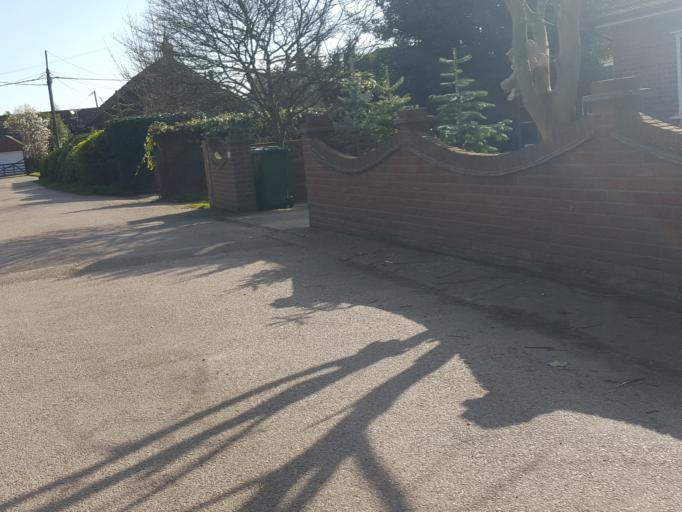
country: GB
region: England
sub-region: Essex
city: Little Clacton
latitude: 51.8596
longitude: 1.1144
